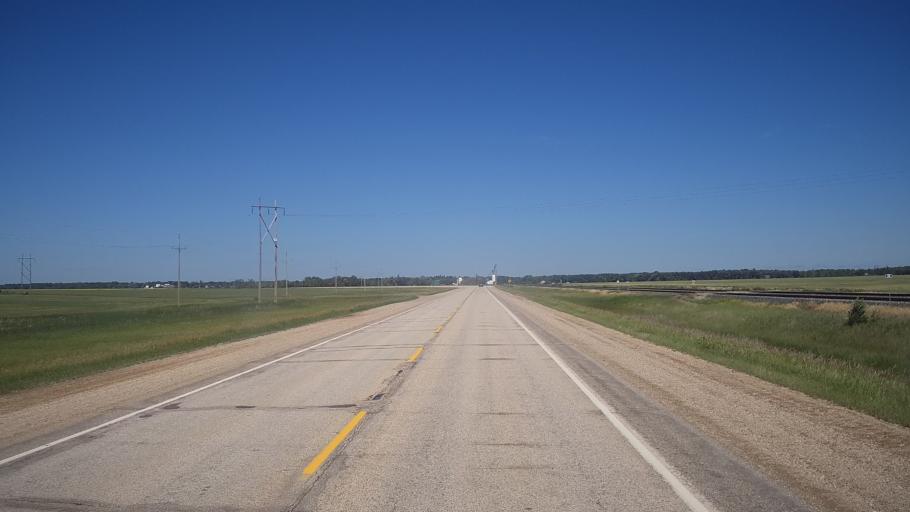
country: CA
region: Manitoba
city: Portage la Prairie
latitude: 50.1219
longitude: -98.5648
